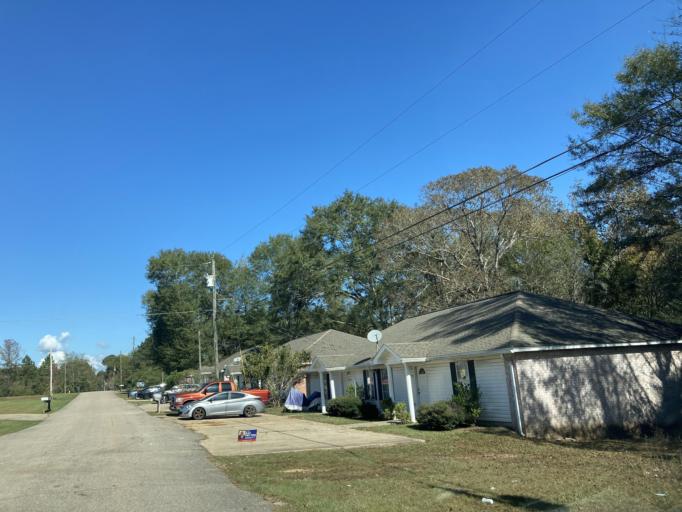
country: US
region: Mississippi
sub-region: Lamar County
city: West Hattiesburg
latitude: 31.2590
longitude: -89.4220
